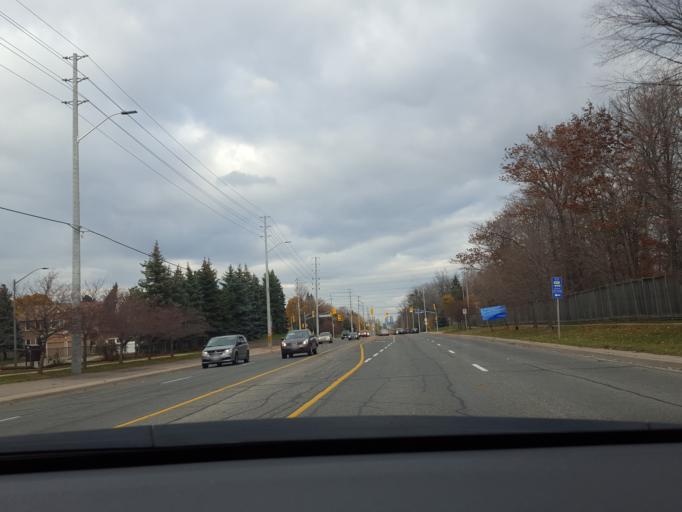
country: CA
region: Ontario
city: Mississauga
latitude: 43.5350
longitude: -79.7014
